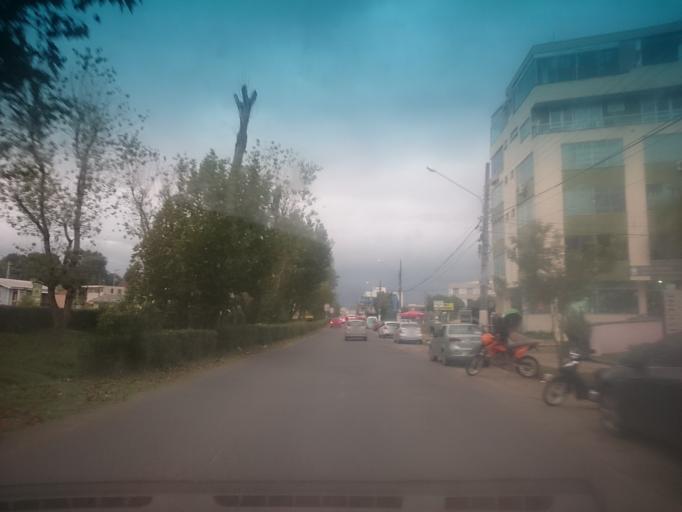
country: BR
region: Santa Catarina
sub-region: Lages
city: Lages
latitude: -27.8092
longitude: -50.3184
